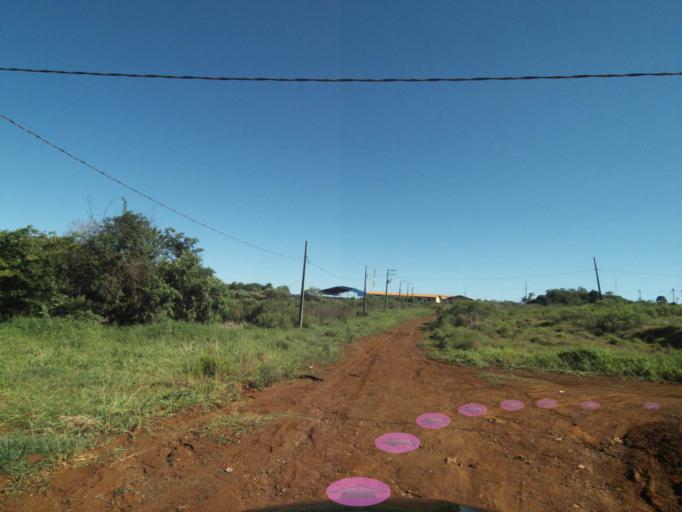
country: BR
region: Parana
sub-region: Coronel Vivida
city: Coronel Vivida
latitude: -26.1369
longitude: -52.3917
